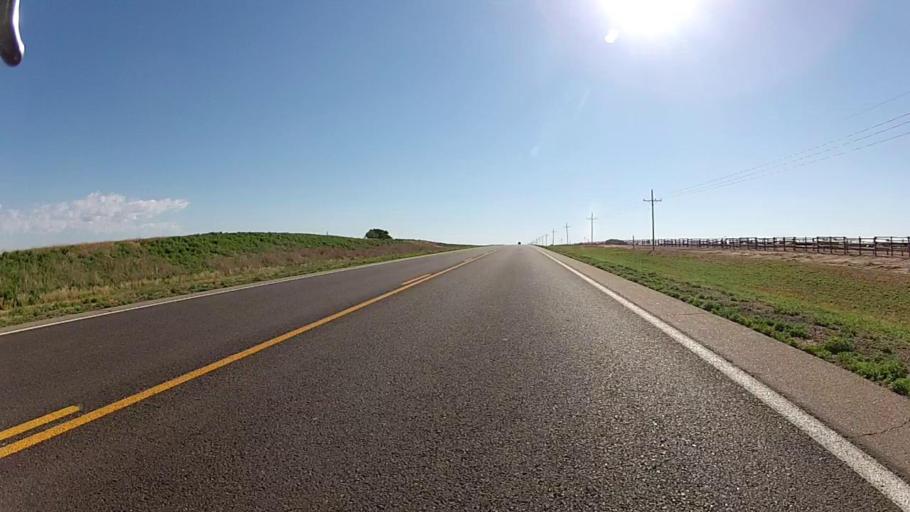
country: US
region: Kansas
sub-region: Haskell County
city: Sublette
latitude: 37.5667
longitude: -100.5509
